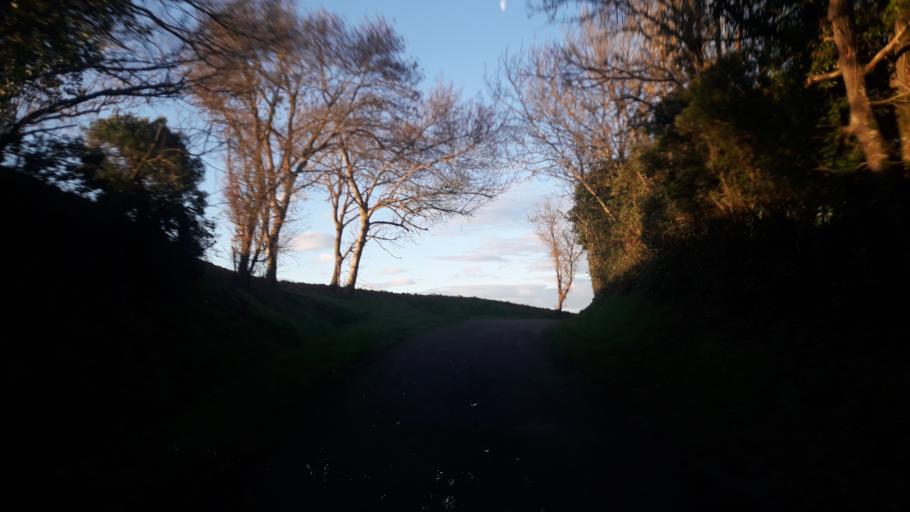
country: FR
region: Midi-Pyrenees
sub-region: Departement du Gers
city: Gimont
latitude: 43.7196
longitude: 0.9729
